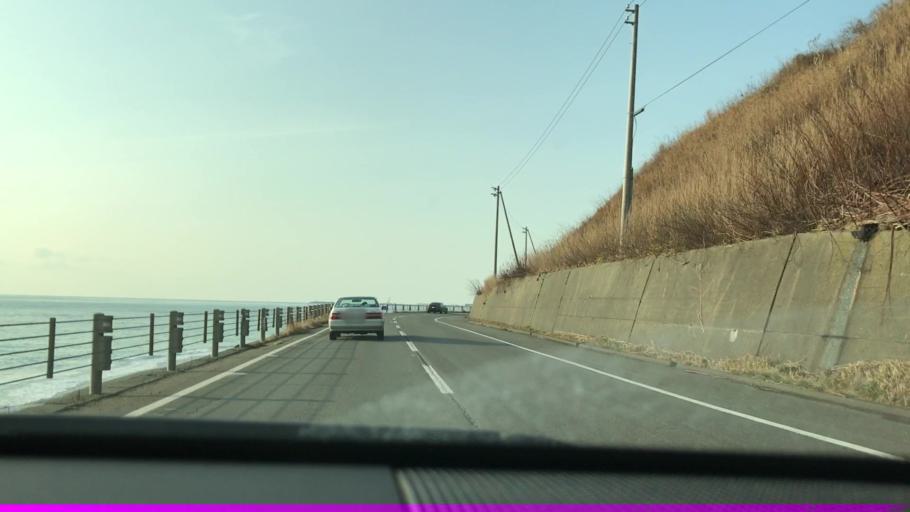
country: JP
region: Hokkaido
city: Shizunai-furukawacho
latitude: 42.2368
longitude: 142.5961
